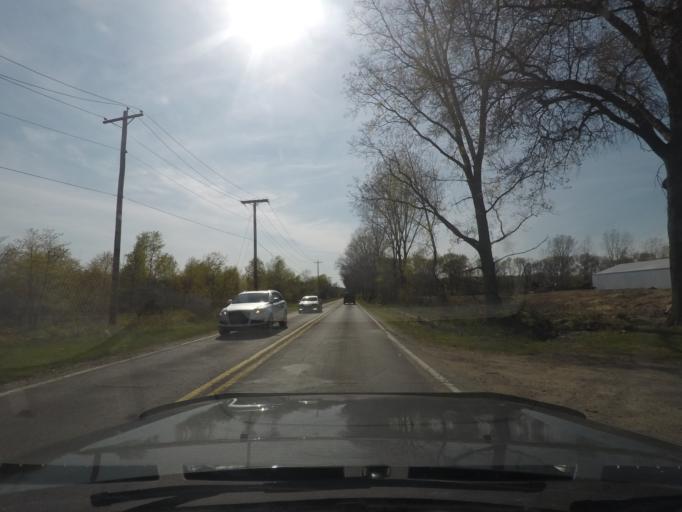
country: US
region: Indiana
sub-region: Saint Joseph County
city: Osceola
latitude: 41.7245
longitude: -86.0425
